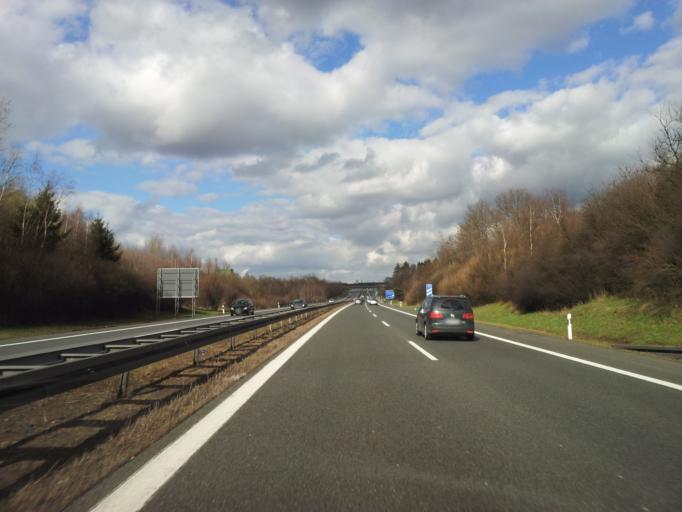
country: DE
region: Saxony
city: Neuensalz
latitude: 50.4964
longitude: 12.1960
